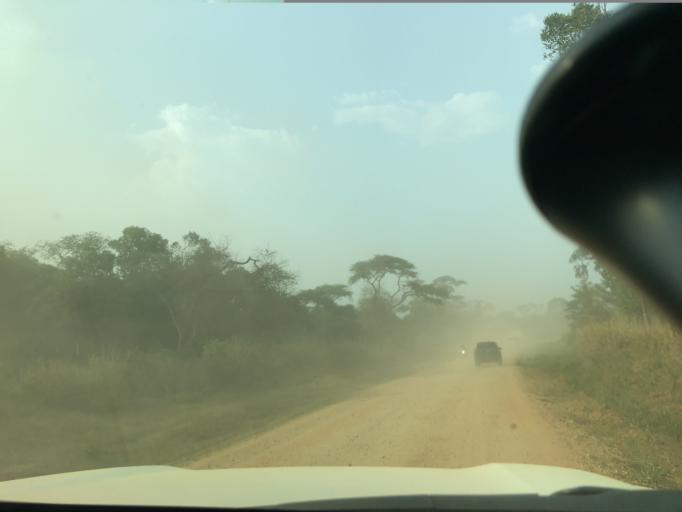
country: CD
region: Nord Kivu
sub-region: North Kivu
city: Butembo
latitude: 0.1205
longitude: 29.6398
